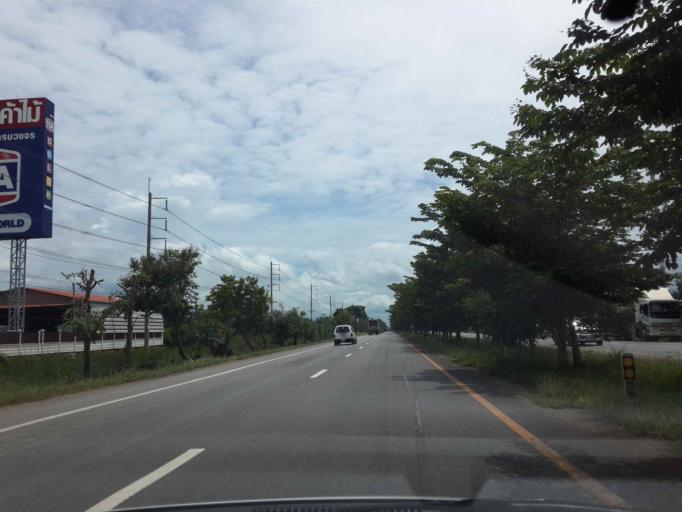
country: TH
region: Ratchaburi
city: Pak Tho
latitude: 13.4040
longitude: 99.8135
